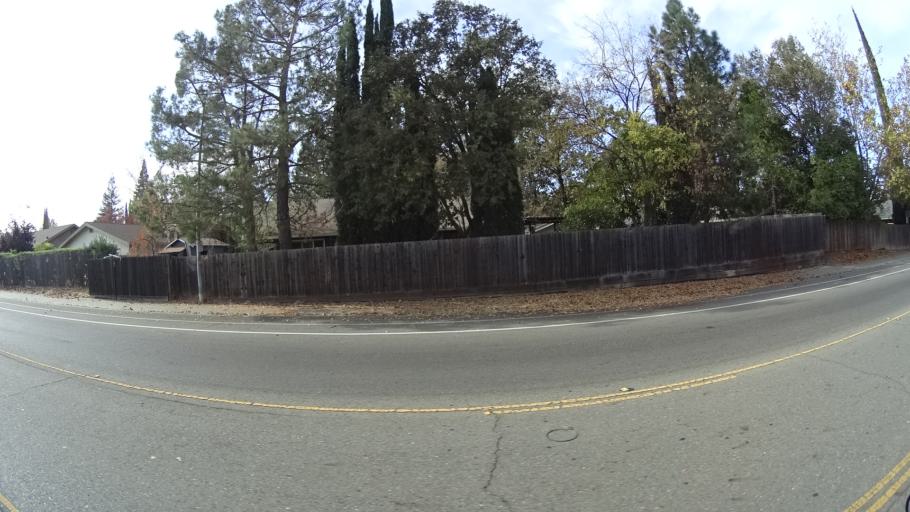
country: US
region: California
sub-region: Sacramento County
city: Citrus Heights
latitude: 38.6950
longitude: -121.2624
